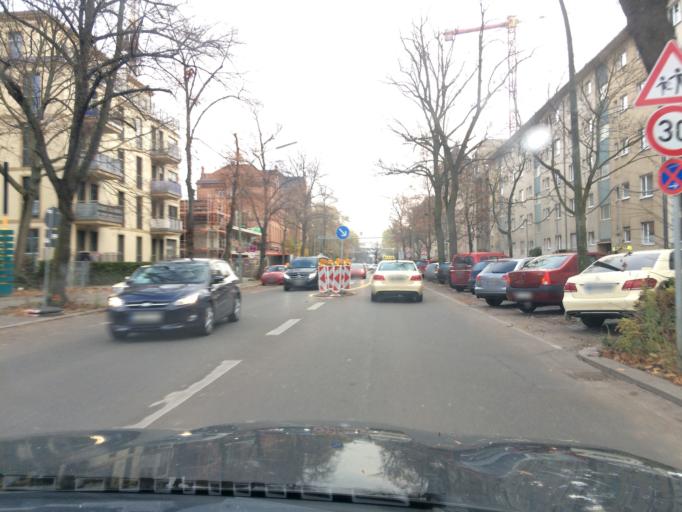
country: DE
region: Berlin
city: Moabit
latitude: 52.5282
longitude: 13.3541
